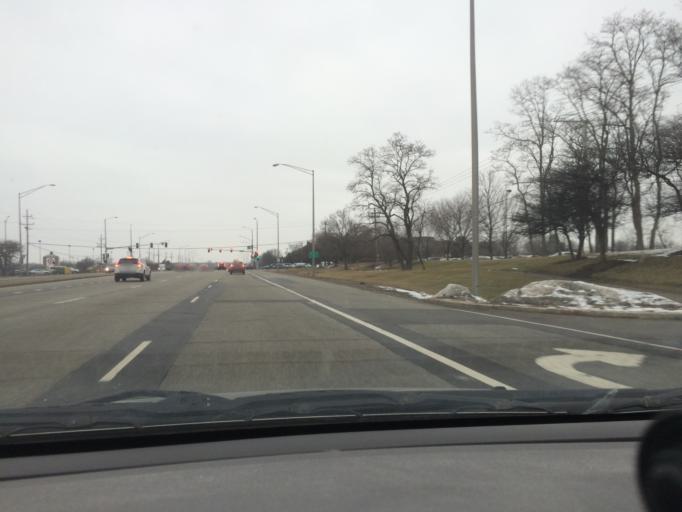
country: US
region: Illinois
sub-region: Cook County
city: Hoffman Estates
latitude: 42.0389
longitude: -88.0431
